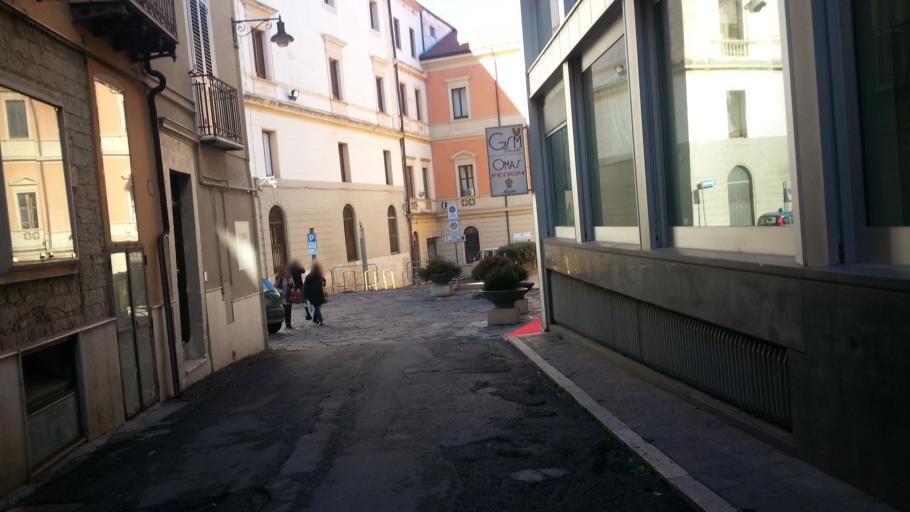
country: IT
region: Basilicate
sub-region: Provincia di Potenza
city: Potenza
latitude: 40.6386
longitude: 15.8028
